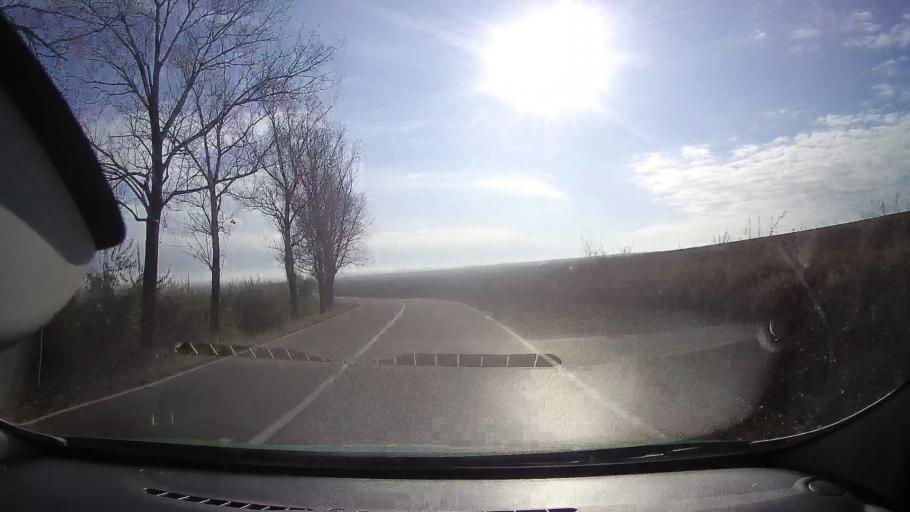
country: RO
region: Tulcea
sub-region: Comuna Mahmudia
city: Mahmudia
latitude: 45.0727
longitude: 29.0931
